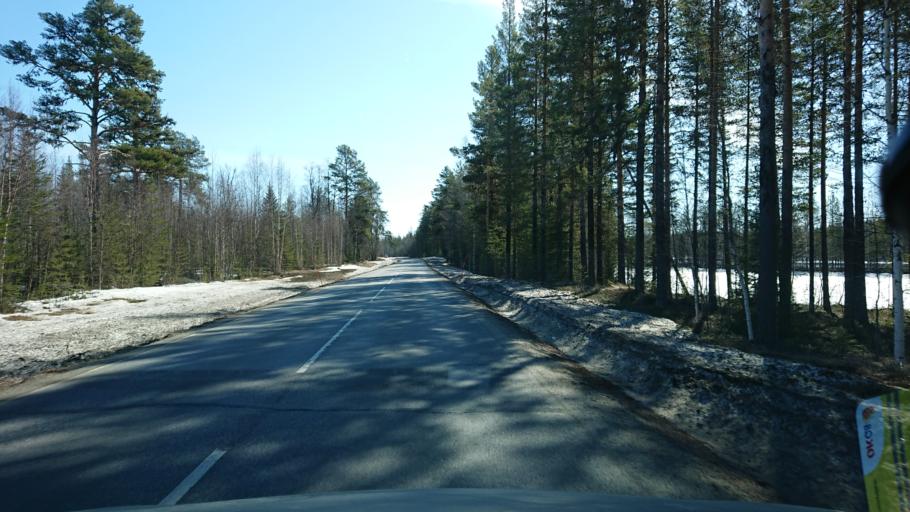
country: SE
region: Vaesterbotten
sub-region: Dorotea Kommun
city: Dorotea
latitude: 64.0089
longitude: 16.2975
